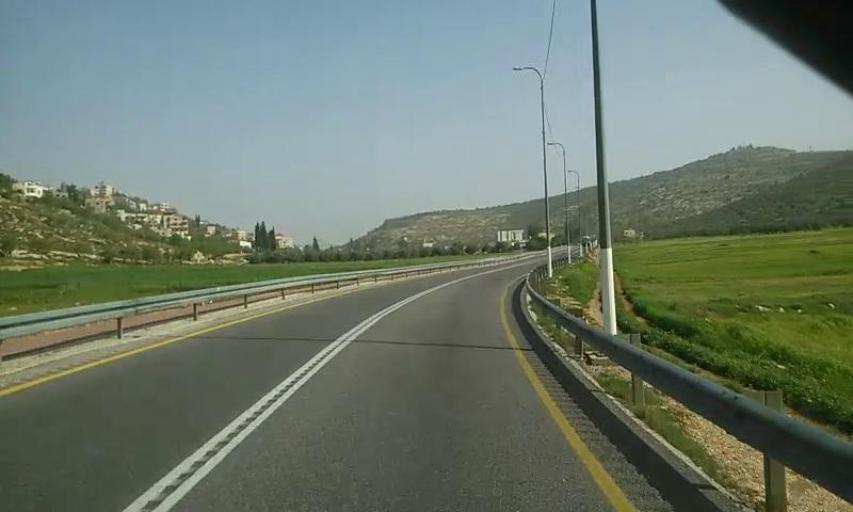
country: PS
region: West Bank
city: As Sawiyah
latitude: 32.0835
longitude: 35.2641
